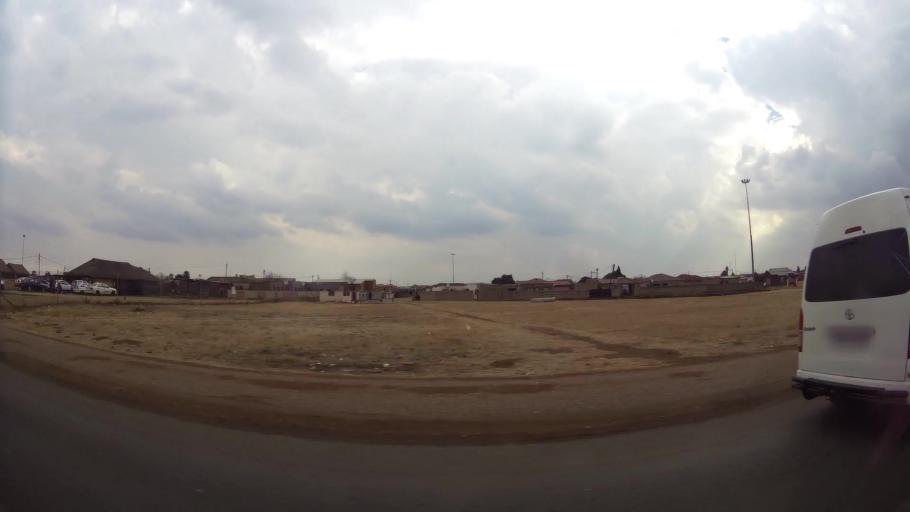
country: ZA
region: Gauteng
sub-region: Ekurhuleni Metropolitan Municipality
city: Germiston
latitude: -26.3822
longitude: 28.1621
